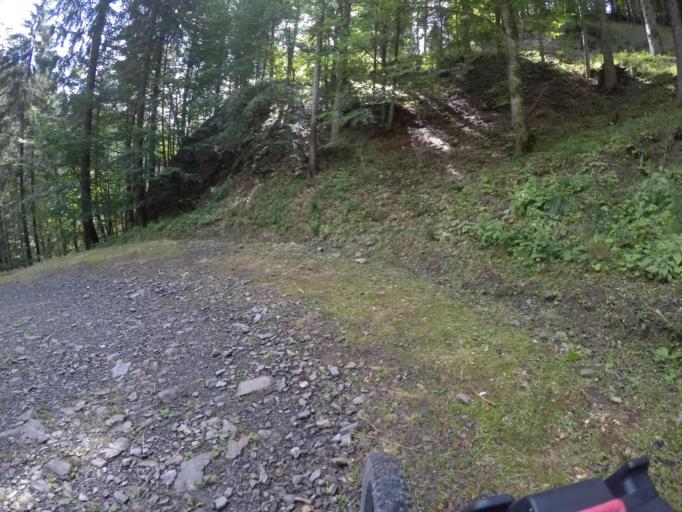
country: IT
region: Friuli Venezia Giulia
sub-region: Provincia di Udine
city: Paularo
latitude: 46.5111
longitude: 13.1854
